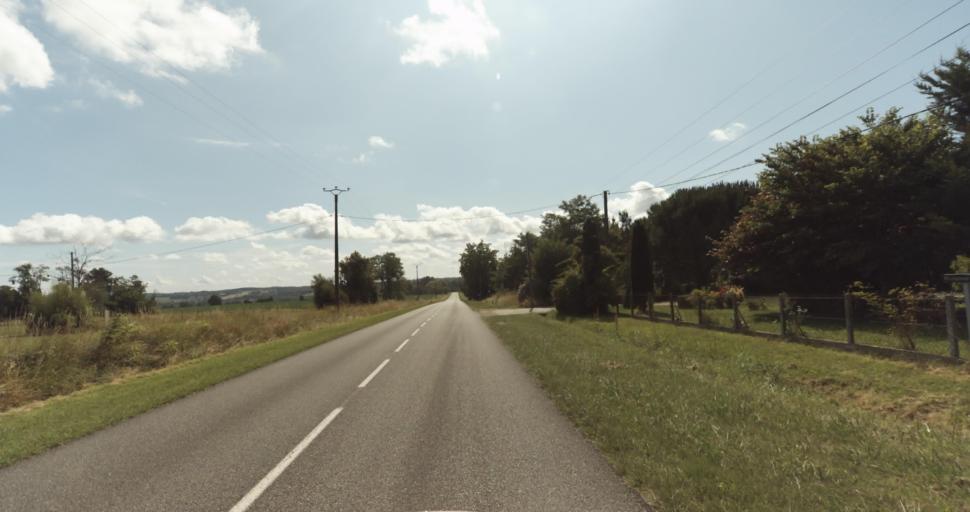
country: FR
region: Aquitaine
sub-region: Departement de la Gironde
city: Bazas
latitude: 44.4408
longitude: -0.1903
